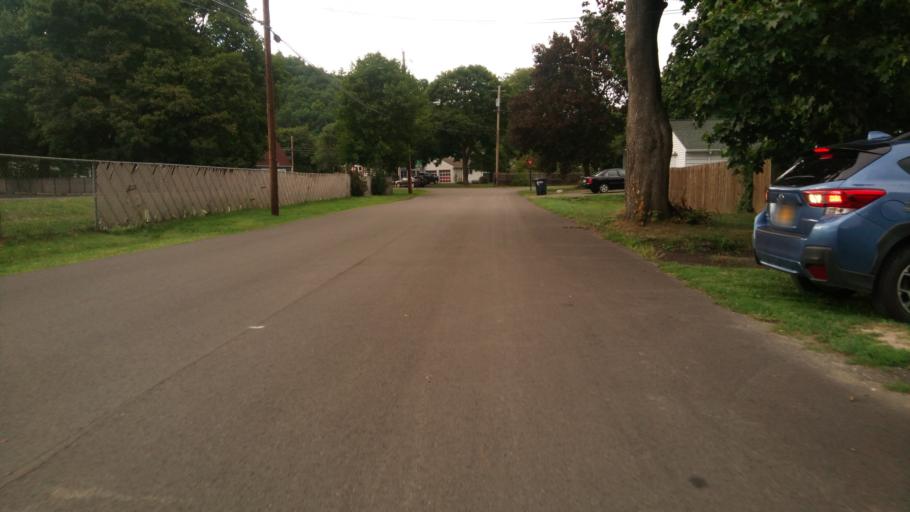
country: US
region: New York
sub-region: Chemung County
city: Southport
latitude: 42.0590
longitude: -76.8170
